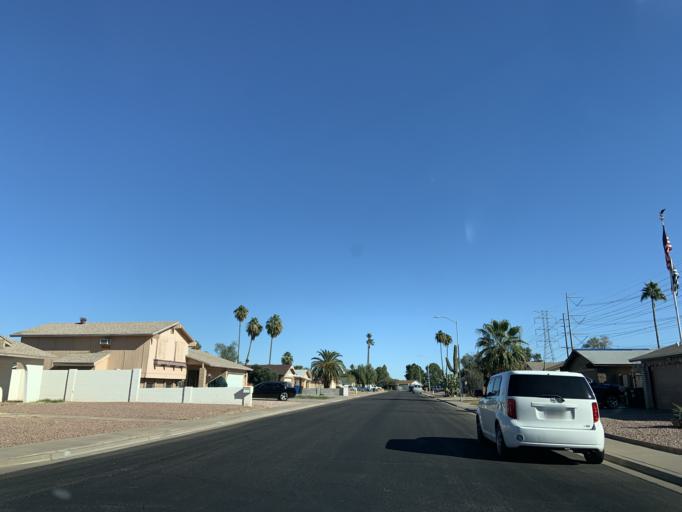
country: US
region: Arizona
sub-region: Maricopa County
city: San Carlos
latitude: 33.3574
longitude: -111.8706
